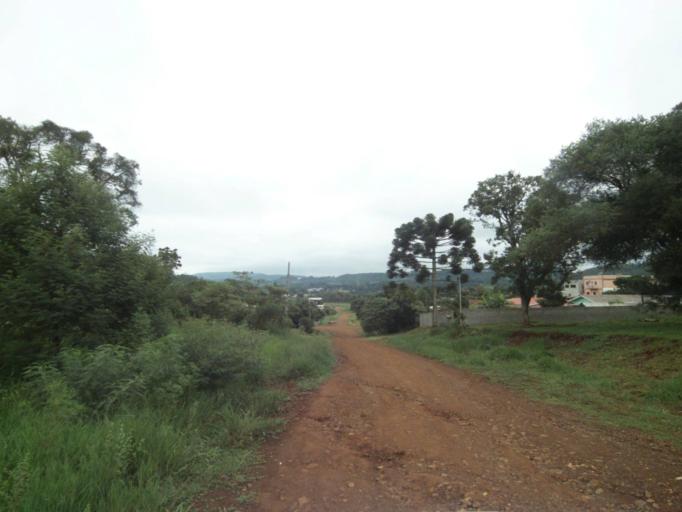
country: BR
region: Parana
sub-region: Pitanga
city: Pitanga
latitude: -24.9395
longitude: -51.8737
